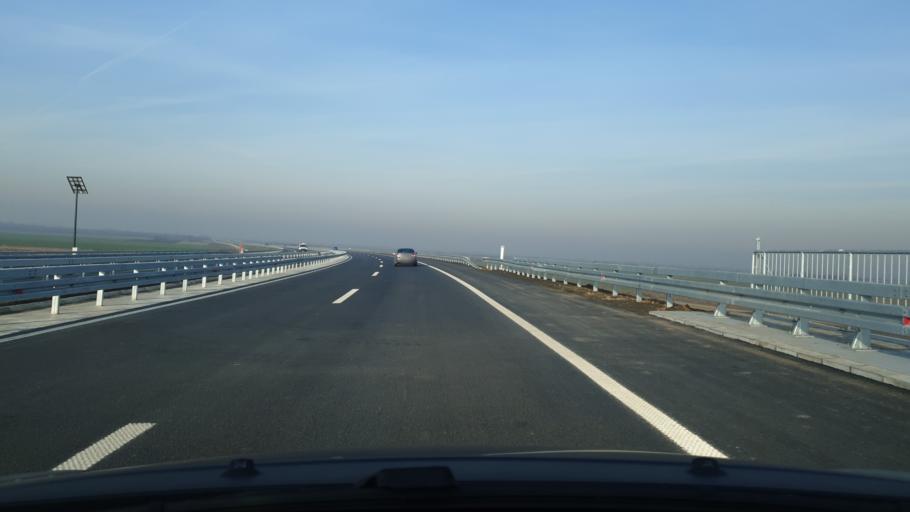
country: RS
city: Umka
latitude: 44.6895
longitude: 20.2674
